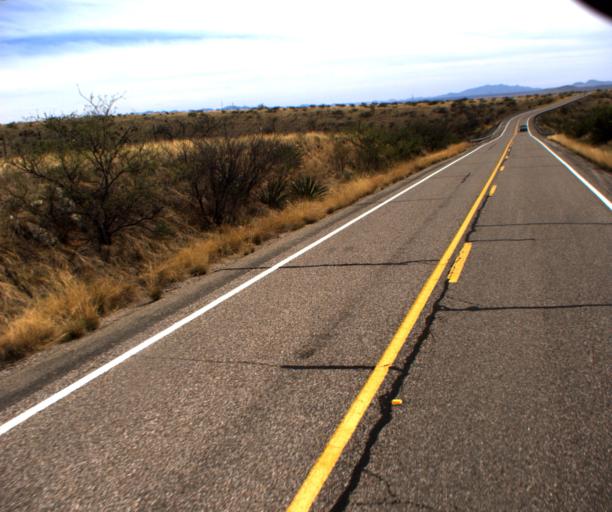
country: US
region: Arizona
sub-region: Cochise County
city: Willcox
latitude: 32.1474
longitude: -109.5650
